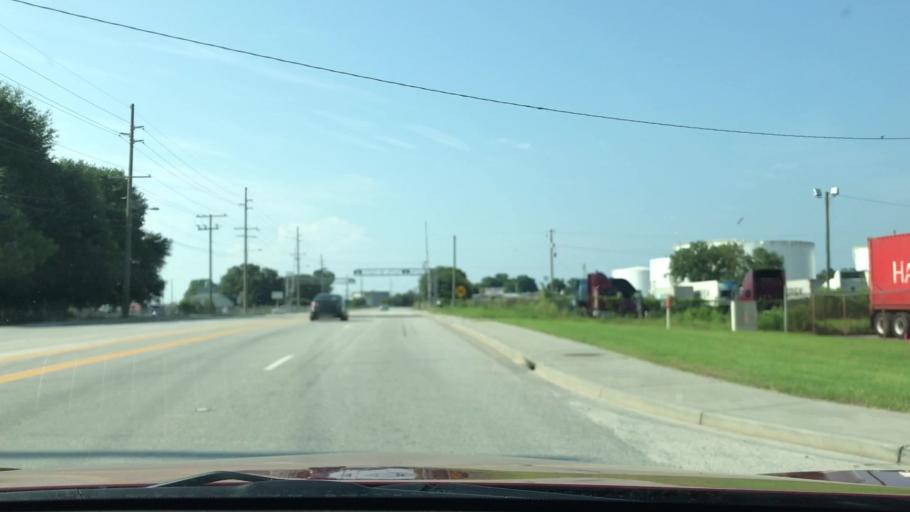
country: US
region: South Carolina
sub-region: Charleston County
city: North Charleston
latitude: 32.8913
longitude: -79.9729
